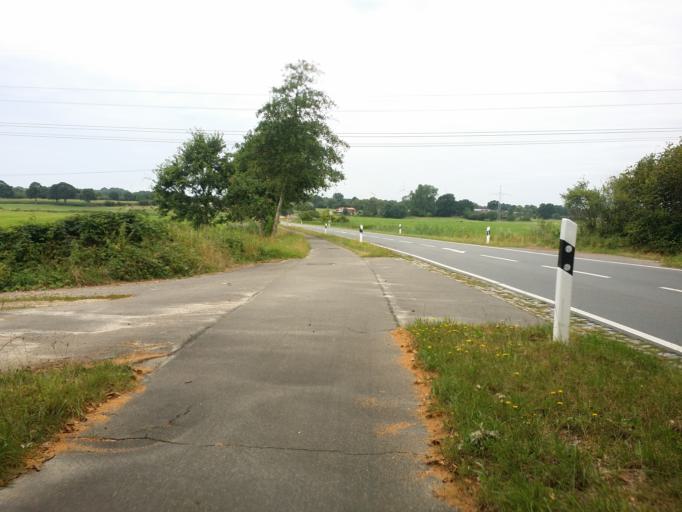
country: DE
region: Schleswig-Holstein
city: Huje
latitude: 53.9690
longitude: 9.4461
